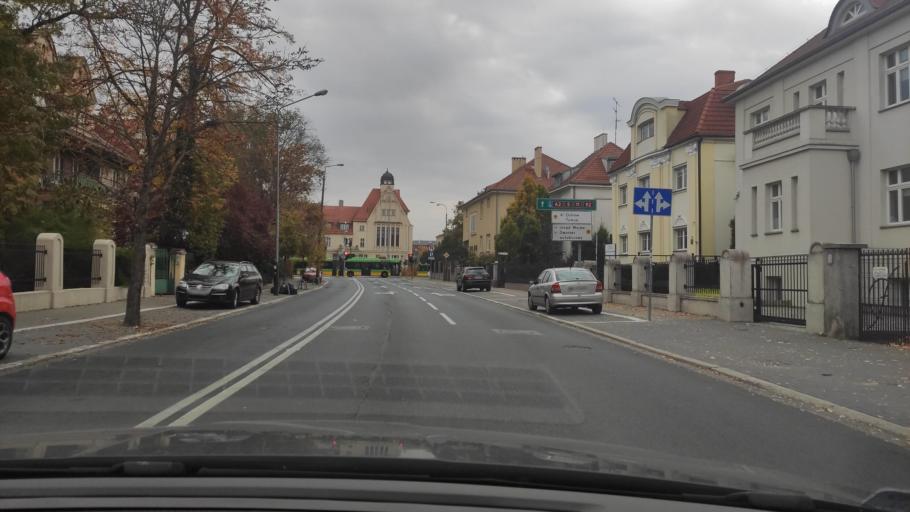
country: PL
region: Greater Poland Voivodeship
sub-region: Poznan
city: Poznan
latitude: 52.4145
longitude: 16.9201
